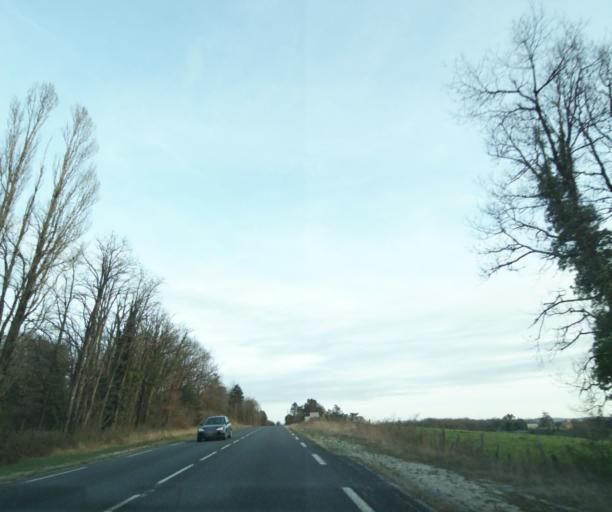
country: FR
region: Midi-Pyrenees
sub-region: Departement du Lot
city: Souillac
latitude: 44.8456
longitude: 1.4587
